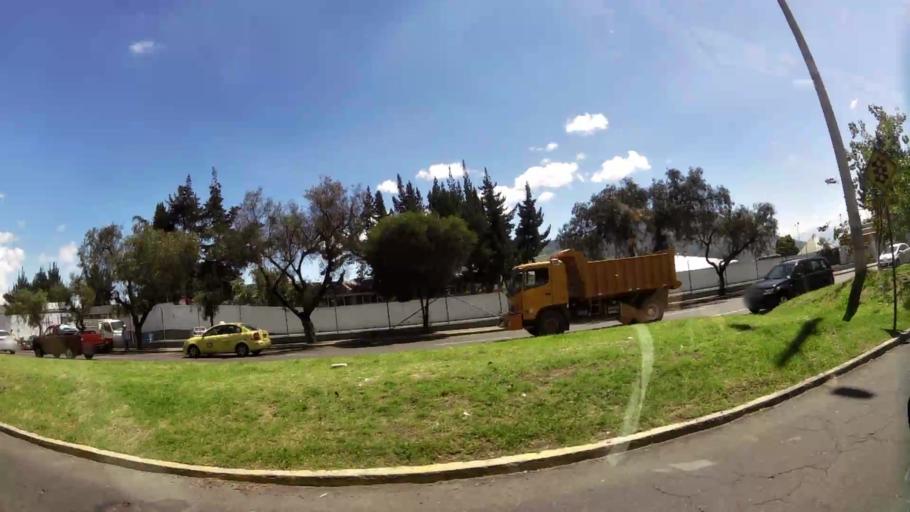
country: EC
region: Pichincha
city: Quito
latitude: -0.0922
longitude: -78.4778
